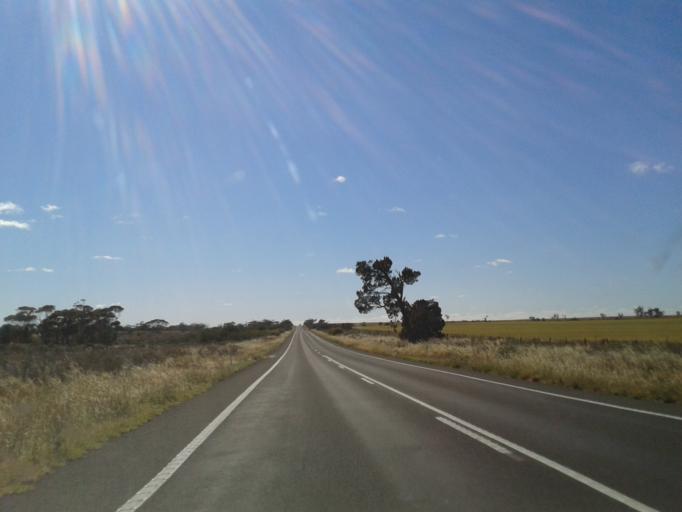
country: AU
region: South Australia
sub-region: Renmark Paringa
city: Renmark
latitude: -34.2748
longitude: 141.2554
